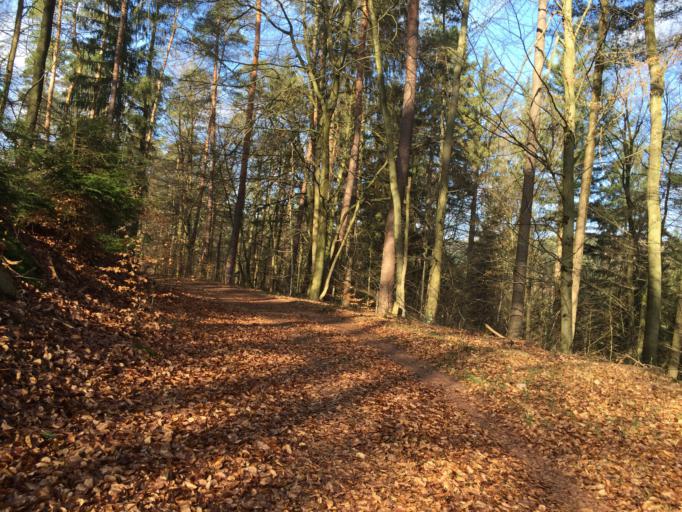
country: DE
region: Rheinland-Pfalz
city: Fischbach
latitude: 49.4219
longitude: 7.9444
